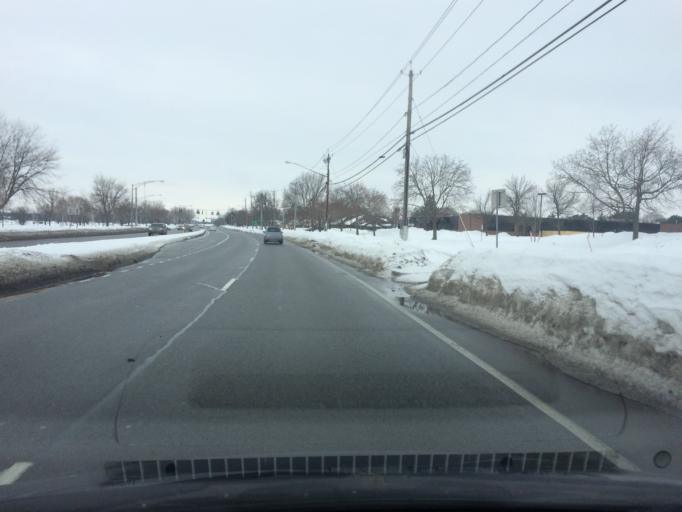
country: US
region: New York
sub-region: Monroe County
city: Rochester
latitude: 43.1047
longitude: -77.6158
